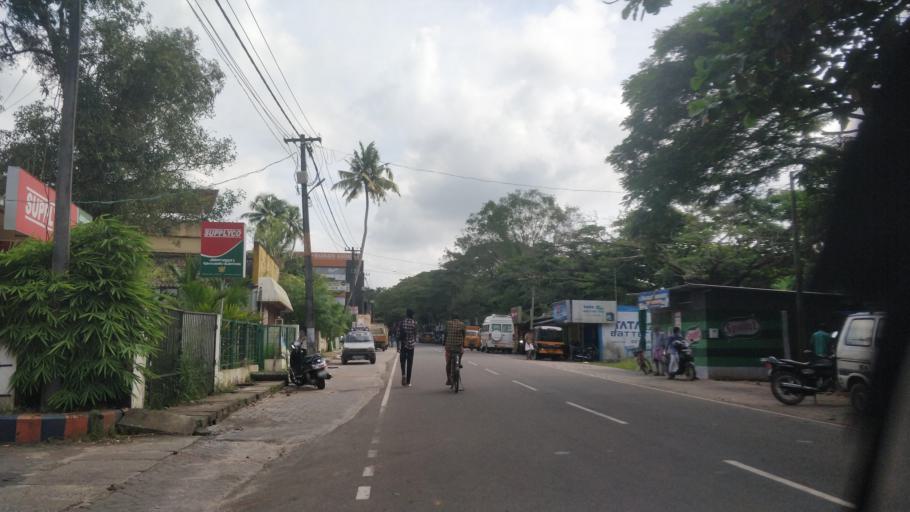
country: IN
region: Kerala
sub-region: Alappuzha
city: Vayalar
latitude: 9.6891
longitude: 76.3405
